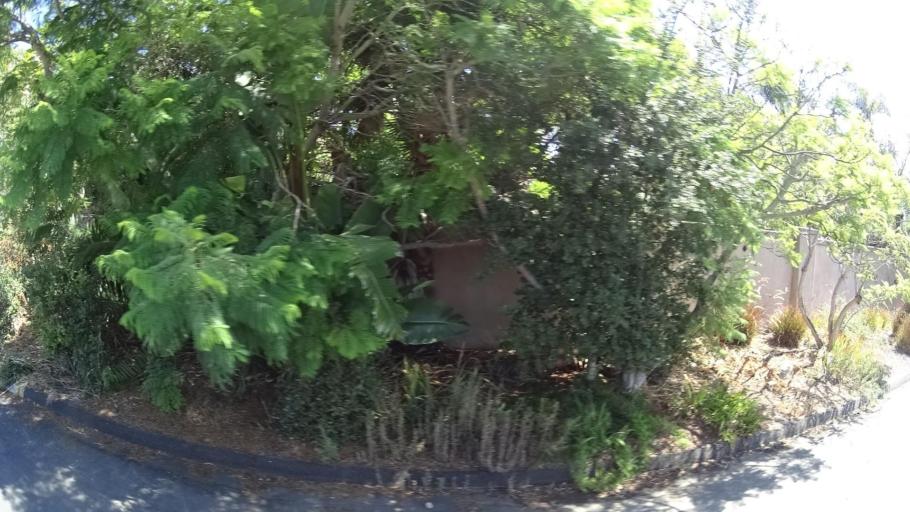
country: US
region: California
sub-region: San Diego County
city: Fairbanks Ranch
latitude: 32.9848
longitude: -117.1792
